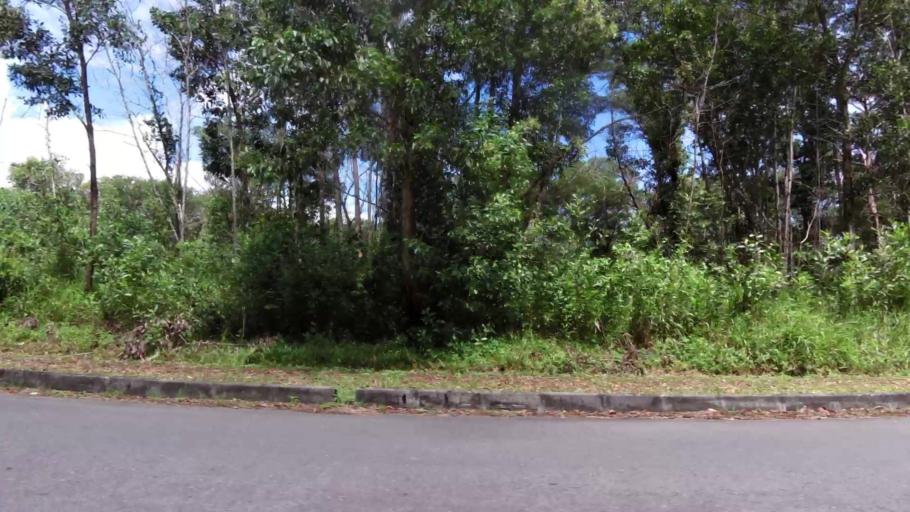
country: BN
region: Brunei and Muara
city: Bandar Seri Begawan
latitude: 4.9518
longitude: 114.9154
